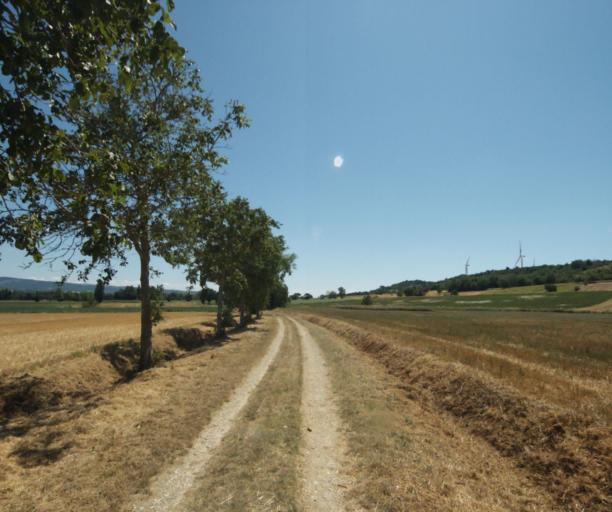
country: FR
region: Midi-Pyrenees
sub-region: Departement de la Haute-Garonne
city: Saint-Felix-Lauragais
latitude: 43.4723
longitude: 1.9233
